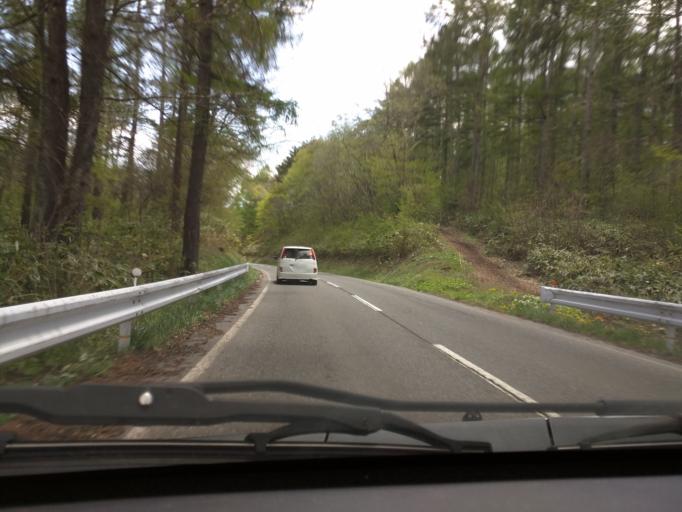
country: JP
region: Nagano
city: Nagano-shi
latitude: 36.7052
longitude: 138.1458
